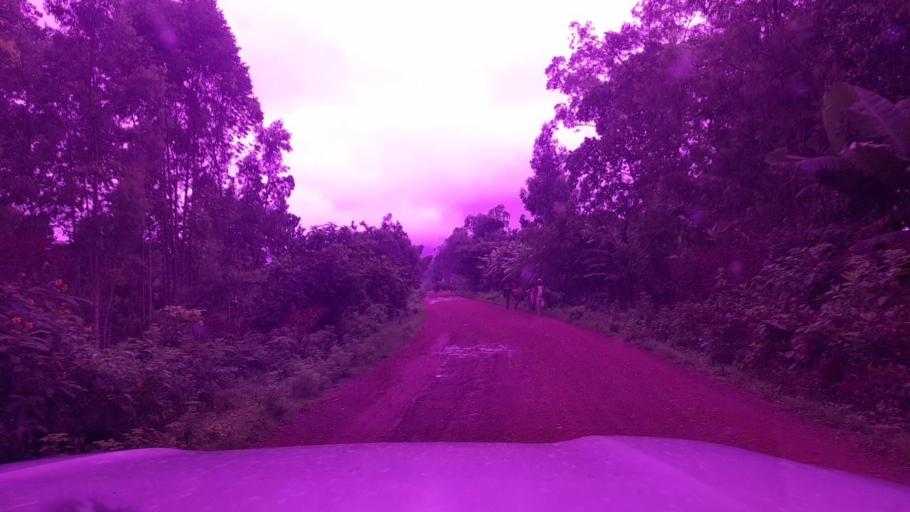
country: ET
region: Southern Nations, Nationalities, and People's Region
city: Bonga
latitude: 7.5906
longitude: 36.0161
